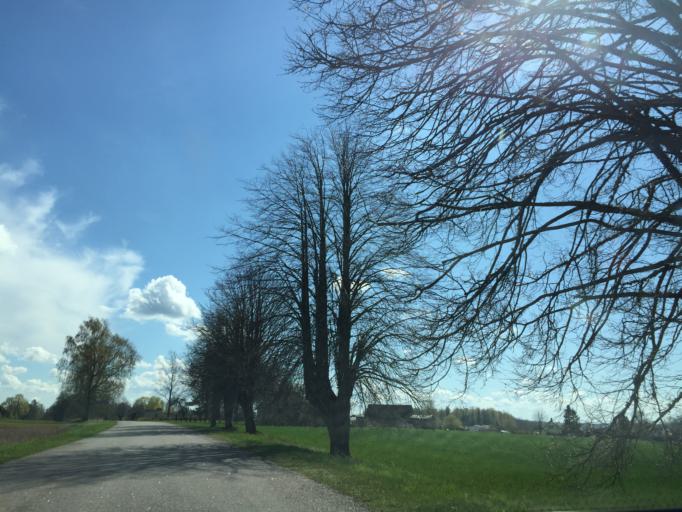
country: LV
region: Strenci
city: Strenci
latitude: 57.5503
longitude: 25.7109
